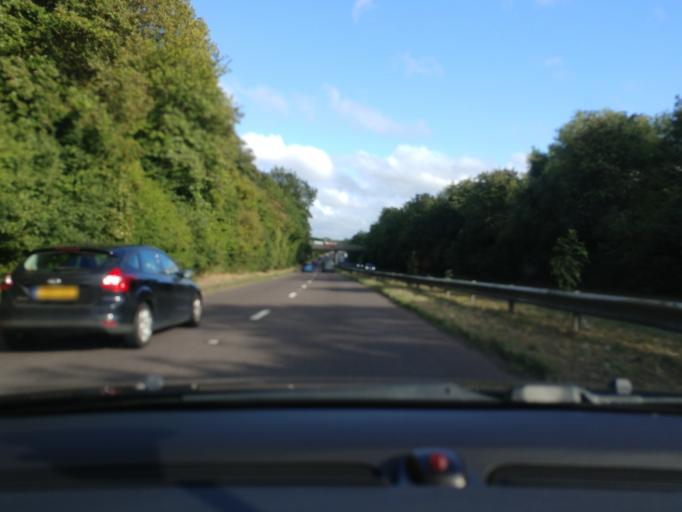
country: GB
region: England
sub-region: Oxfordshire
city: Cowley
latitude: 51.7176
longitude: -1.2309
